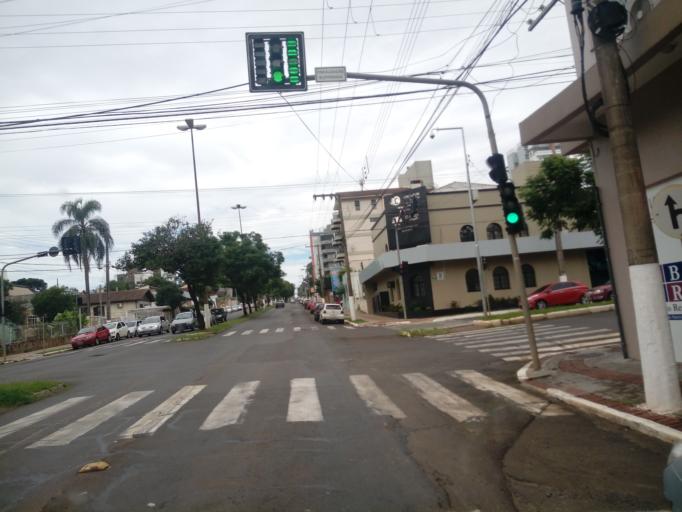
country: BR
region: Santa Catarina
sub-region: Chapeco
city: Chapeco
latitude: -27.1039
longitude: -52.6198
